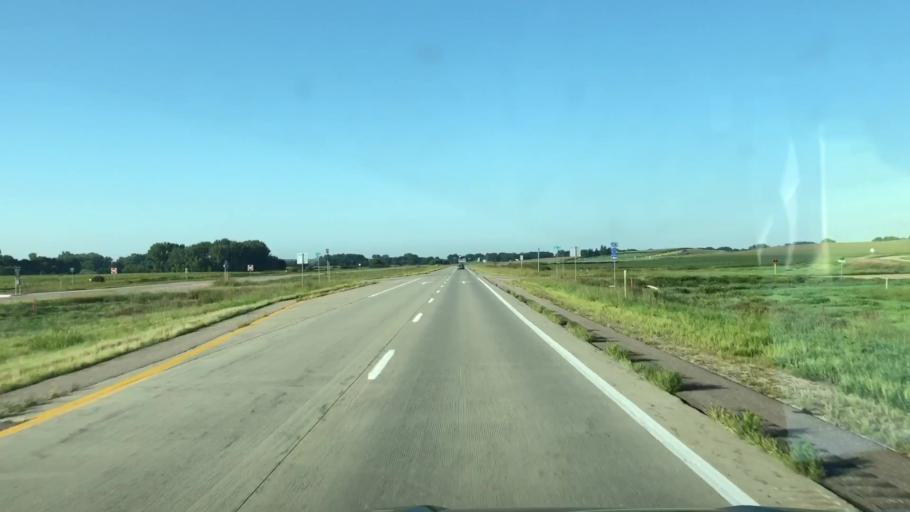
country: US
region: Iowa
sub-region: Plymouth County
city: Le Mars
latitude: 42.8676
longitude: -96.1141
